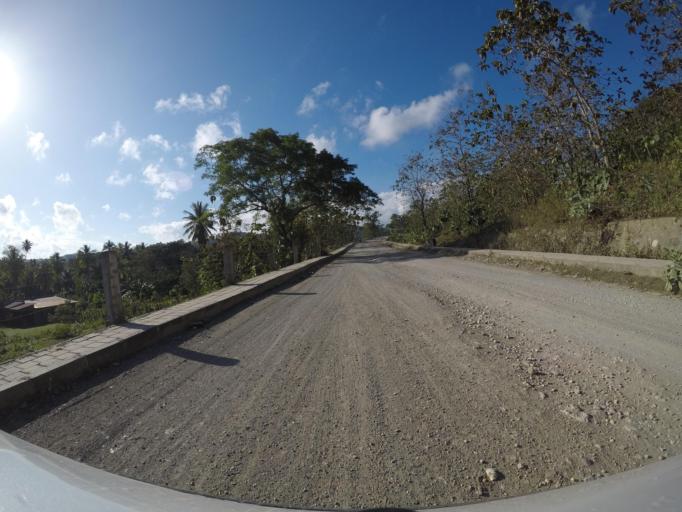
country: TL
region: Viqueque
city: Viqueque
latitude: -8.8442
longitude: 126.3695
